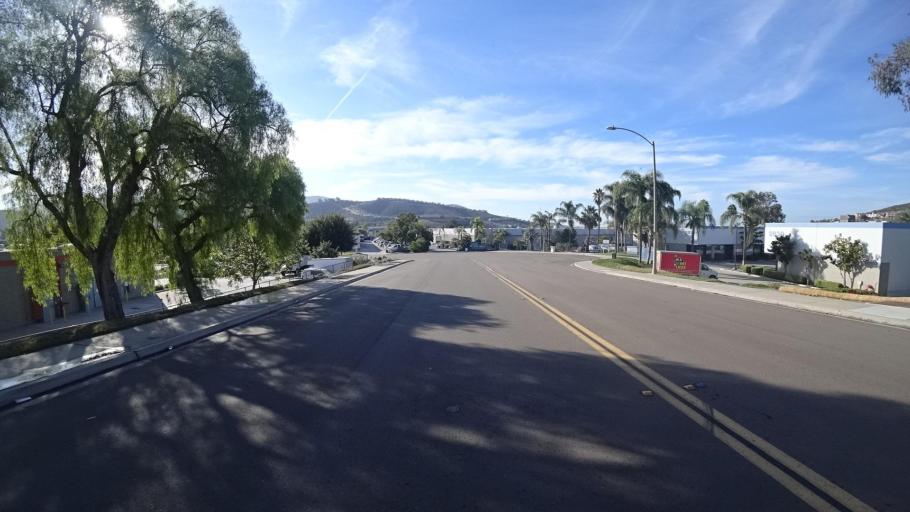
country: US
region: California
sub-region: San Diego County
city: Spring Valley
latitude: 32.7297
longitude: -116.9690
